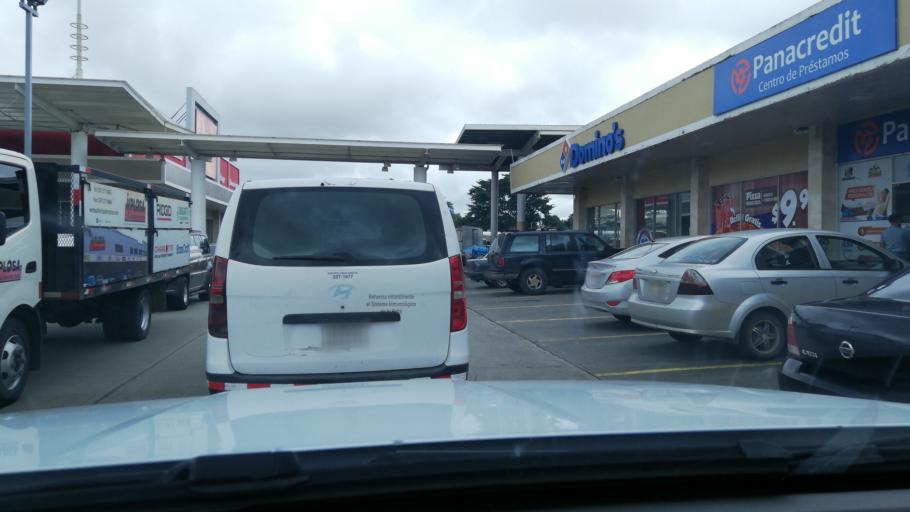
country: PA
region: Panama
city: Tocumen
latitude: 9.1052
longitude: -79.3705
